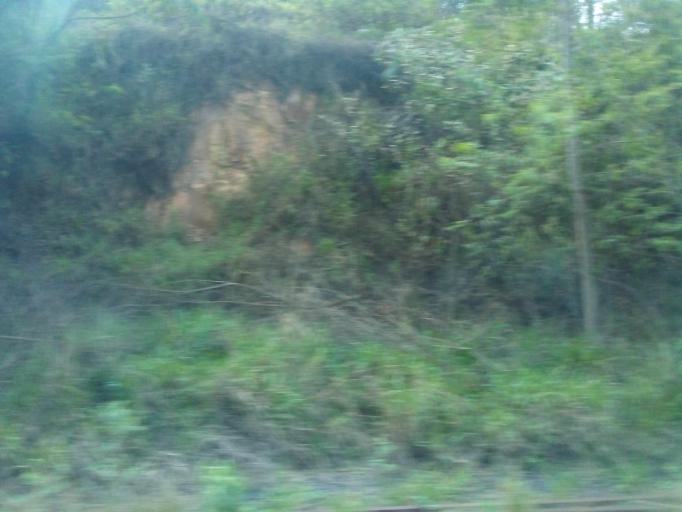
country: BR
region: Minas Gerais
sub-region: Raposos
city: Raposos
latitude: -19.8720
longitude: -43.7907
